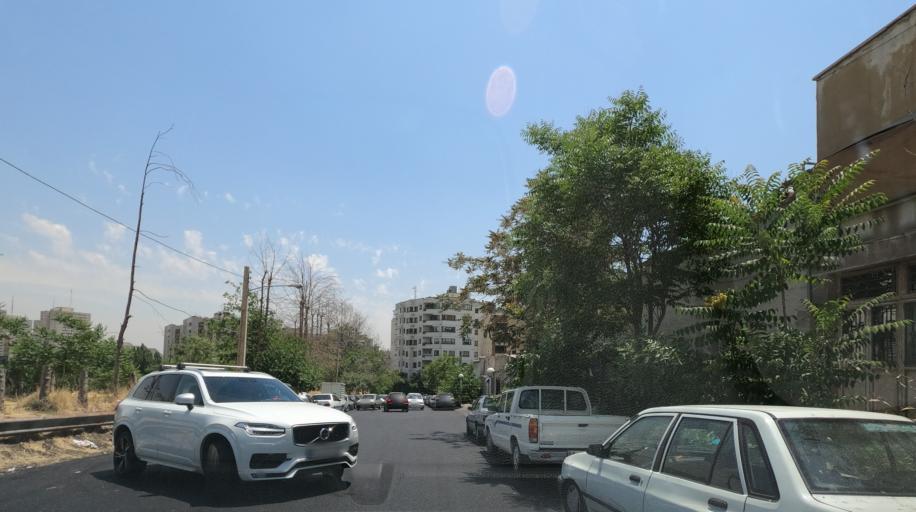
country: IR
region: Tehran
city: Tajrish
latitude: 35.7918
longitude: 51.3850
